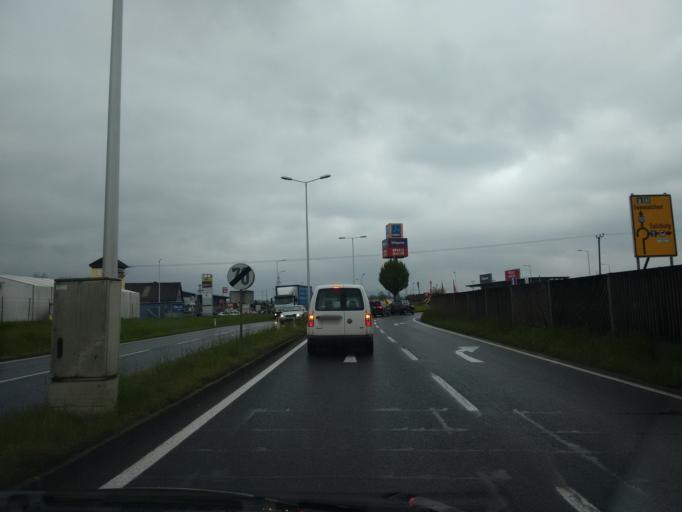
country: AT
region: Upper Austria
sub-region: Politischer Bezirk Vocklabruck
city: Timelkam
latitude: 47.9992
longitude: 13.6229
